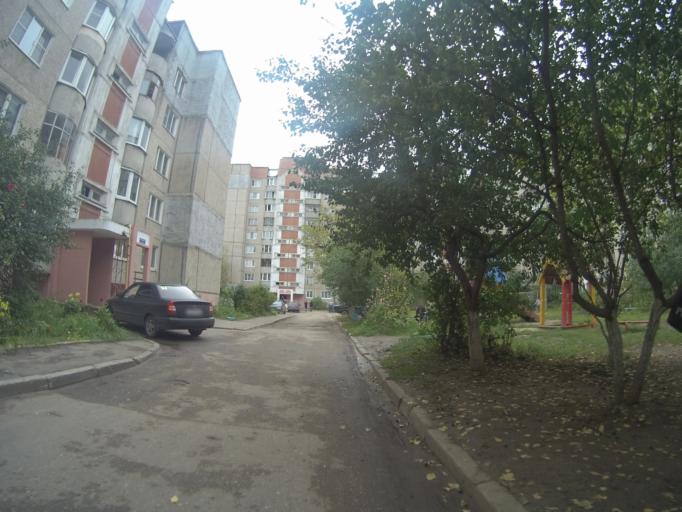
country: RU
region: Vladimir
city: Vladimir
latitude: 56.1160
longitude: 40.3543
